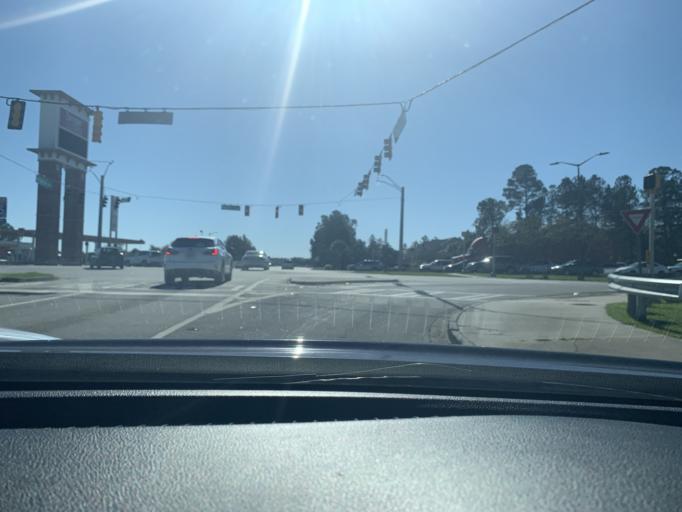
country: US
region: Georgia
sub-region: Chatham County
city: Pooler
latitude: 32.1410
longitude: -81.2473
